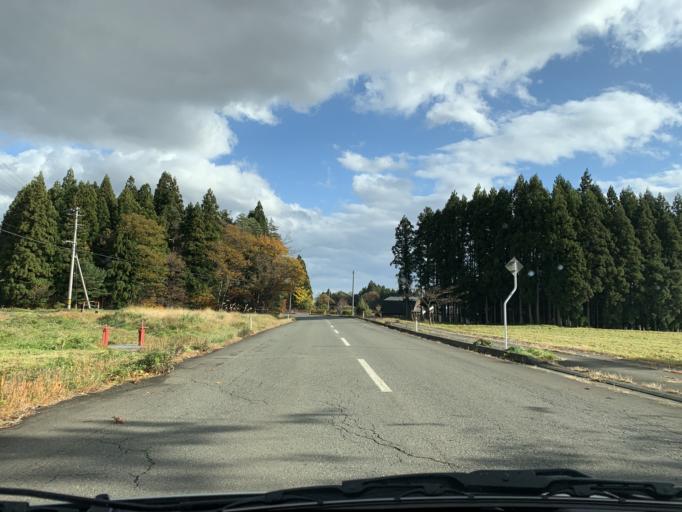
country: JP
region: Iwate
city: Mizusawa
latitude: 39.1153
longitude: 141.0055
